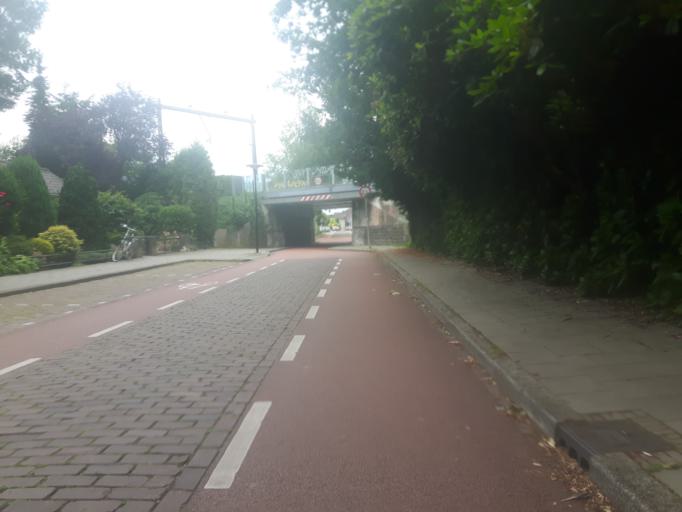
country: NL
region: Overijssel
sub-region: Gemeente Hengelo
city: Hengelo
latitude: 52.2640
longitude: 6.8078
